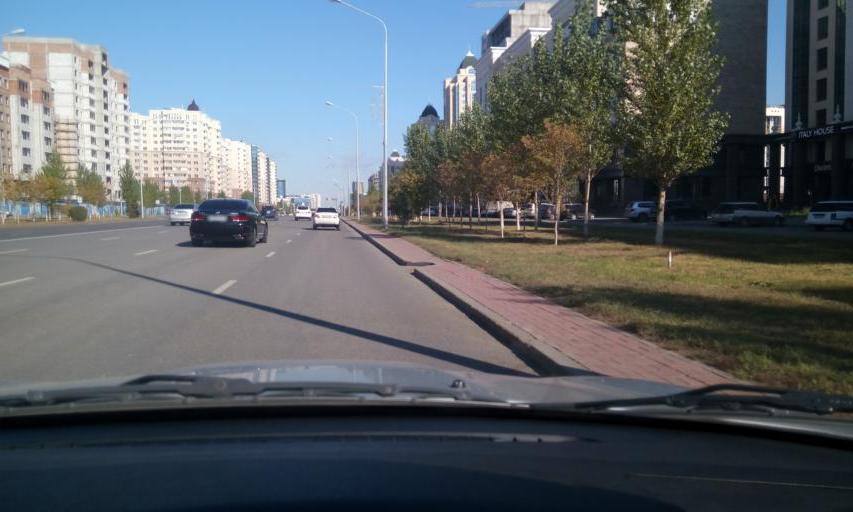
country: KZ
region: Astana Qalasy
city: Astana
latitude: 51.1103
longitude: 71.4324
